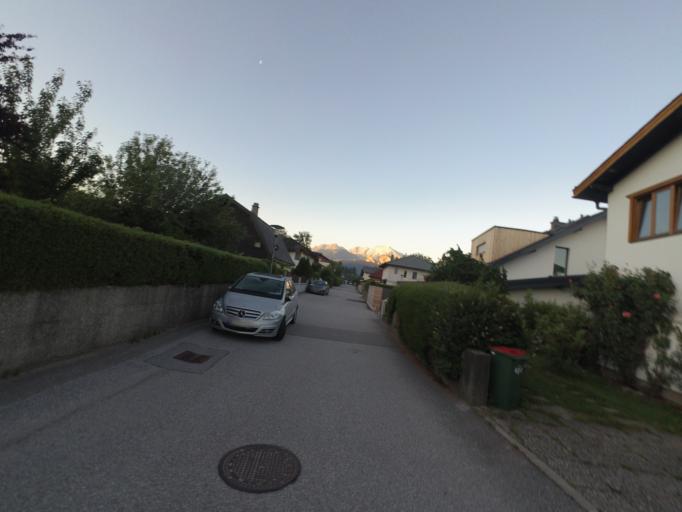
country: AT
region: Salzburg
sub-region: Politischer Bezirk Hallein
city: Puch bei Hallein
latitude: 47.7259
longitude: 13.0788
